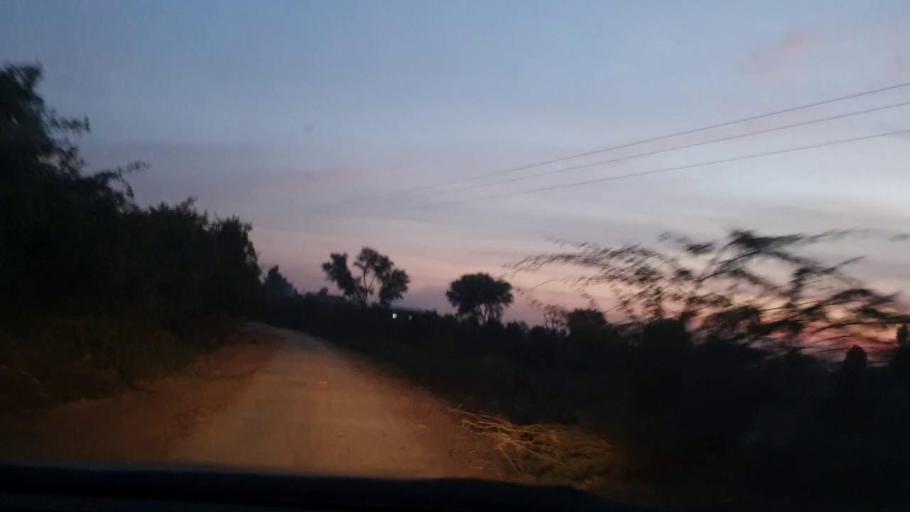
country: PK
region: Sindh
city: Sakrand
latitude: 26.1885
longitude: 68.3014
